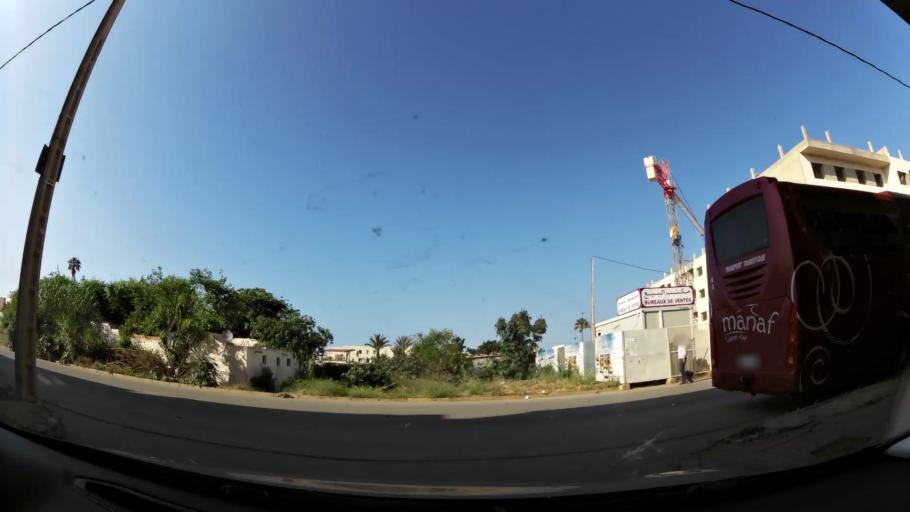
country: MA
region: Rabat-Sale-Zemmour-Zaer
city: Sale
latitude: 34.0481
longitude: -6.8136
